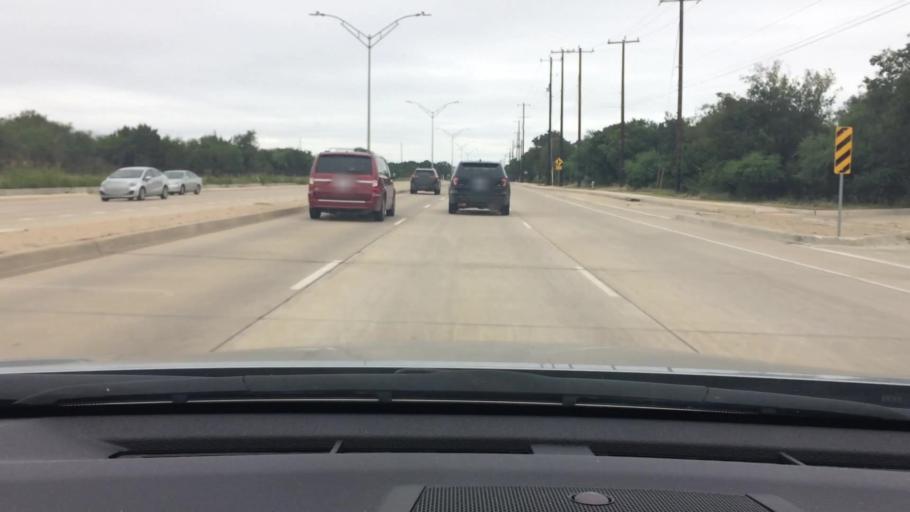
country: US
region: Texas
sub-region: Bexar County
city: Hollywood Park
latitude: 29.6180
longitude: -98.4226
